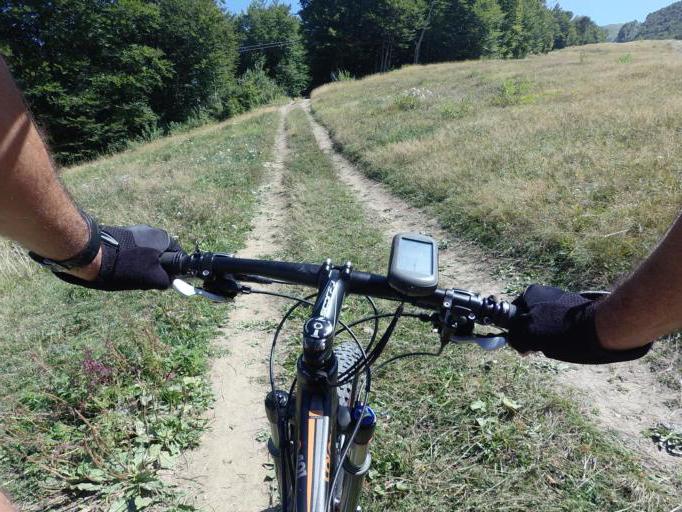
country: IT
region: Emilia-Romagna
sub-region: Provincia di Modena
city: Montecreto
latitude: 44.2154
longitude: 10.6919
